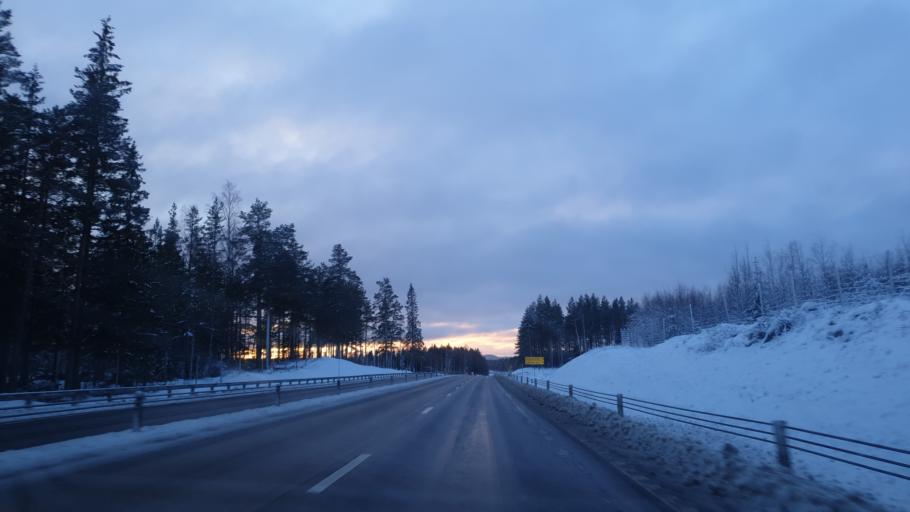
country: SE
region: Vaesterbotten
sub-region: Nordmalings Kommun
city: Nordmaling
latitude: 63.4878
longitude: 19.3092
